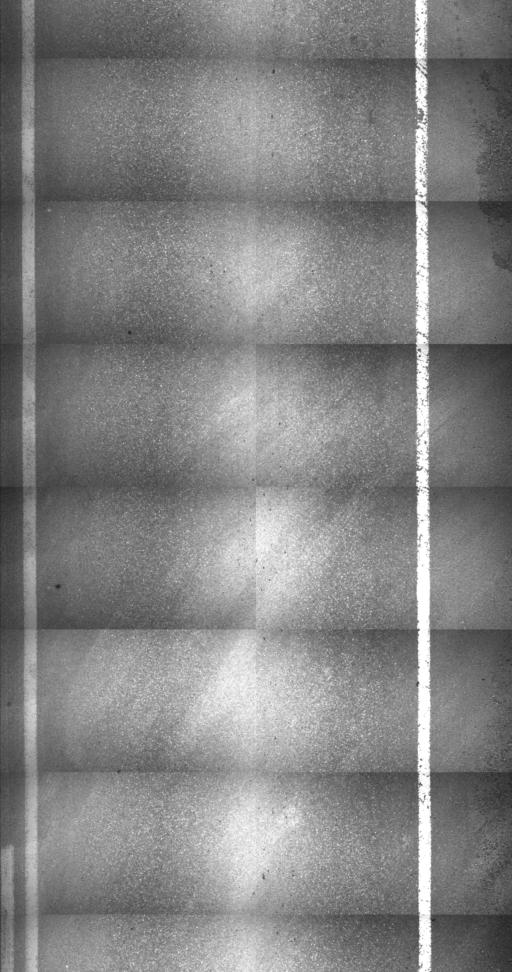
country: US
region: Vermont
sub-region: Chittenden County
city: Jericho
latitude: 44.5249
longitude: -73.0316
